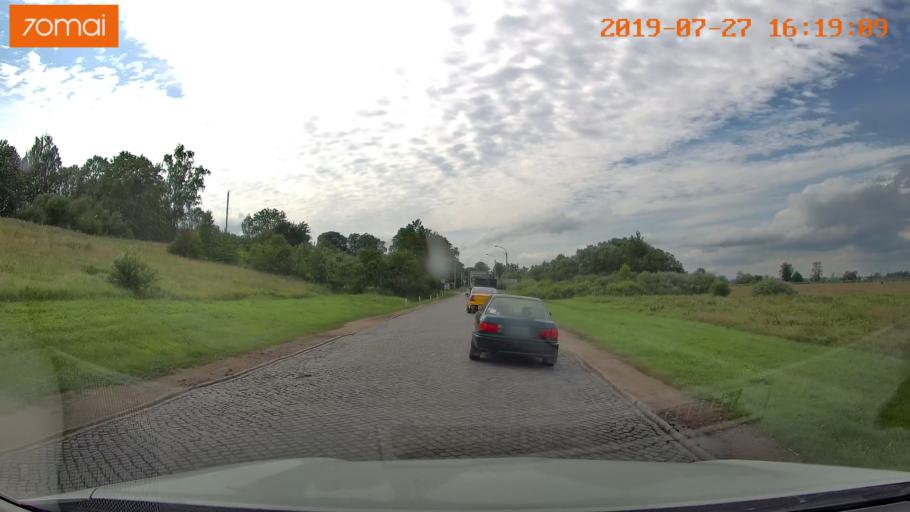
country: RU
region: Kaliningrad
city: Chernyakhovsk
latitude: 54.6255
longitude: 21.5333
